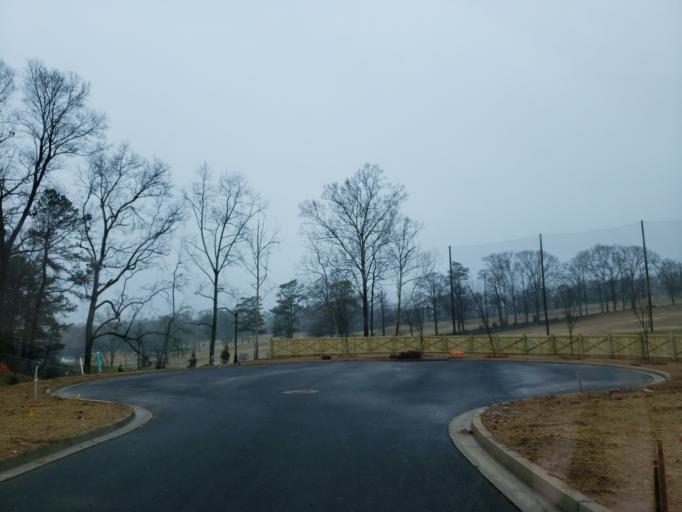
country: US
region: Georgia
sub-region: Cobb County
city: Marietta
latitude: 33.9401
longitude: -84.5568
